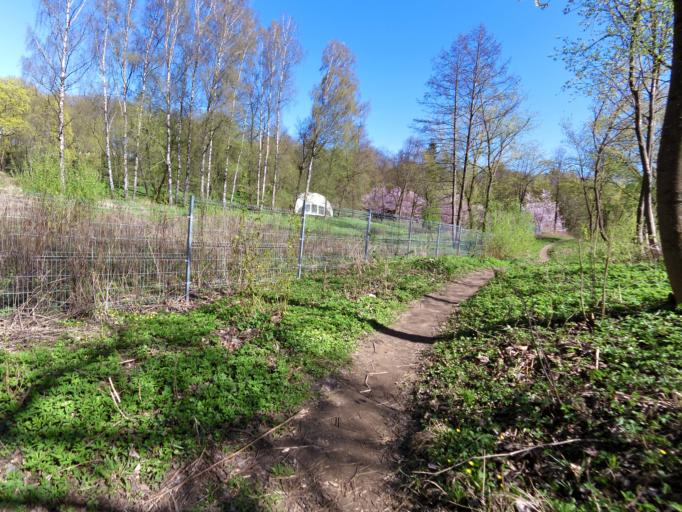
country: LT
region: Vilnius County
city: Vilkpede
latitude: 54.6817
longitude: 25.2312
